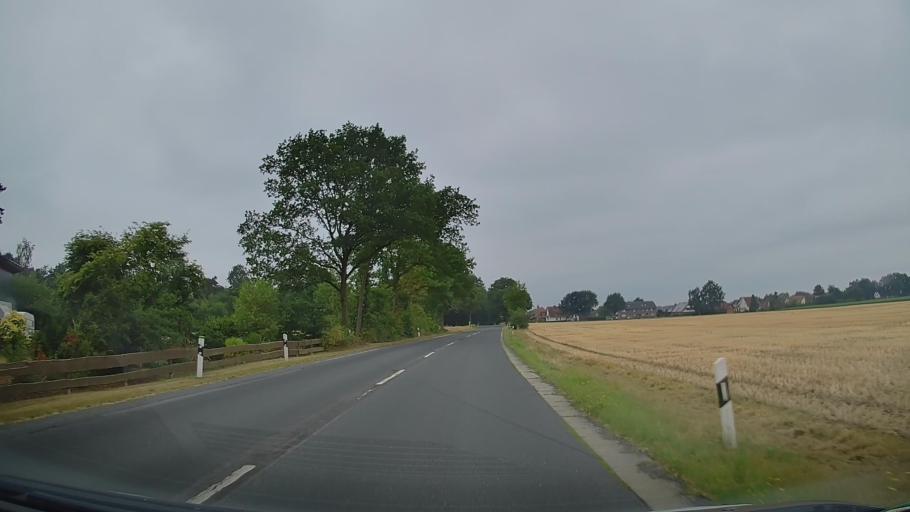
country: DE
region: North Rhine-Westphalia
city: Rahden
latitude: 52.4639
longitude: 8.5516
